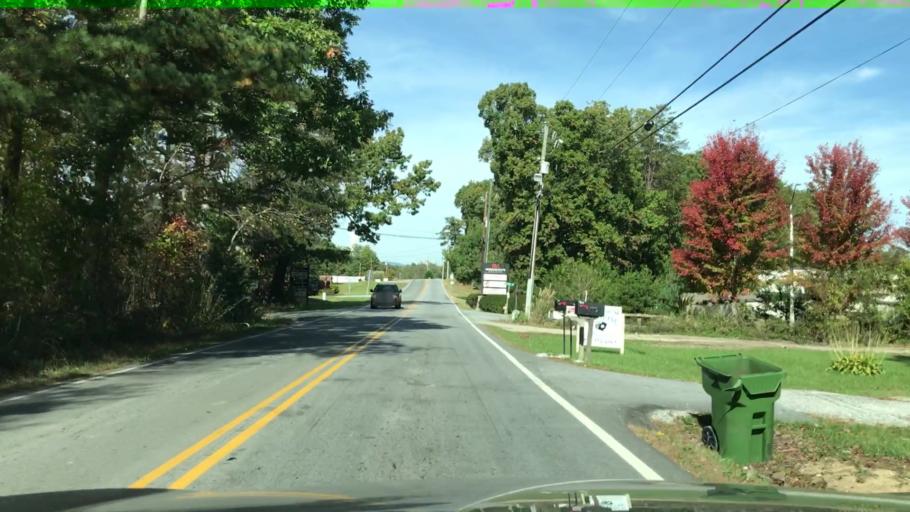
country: US
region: North Carolina
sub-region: Buncombe County
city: Royal Pines
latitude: 35.4559
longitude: -82.5277
